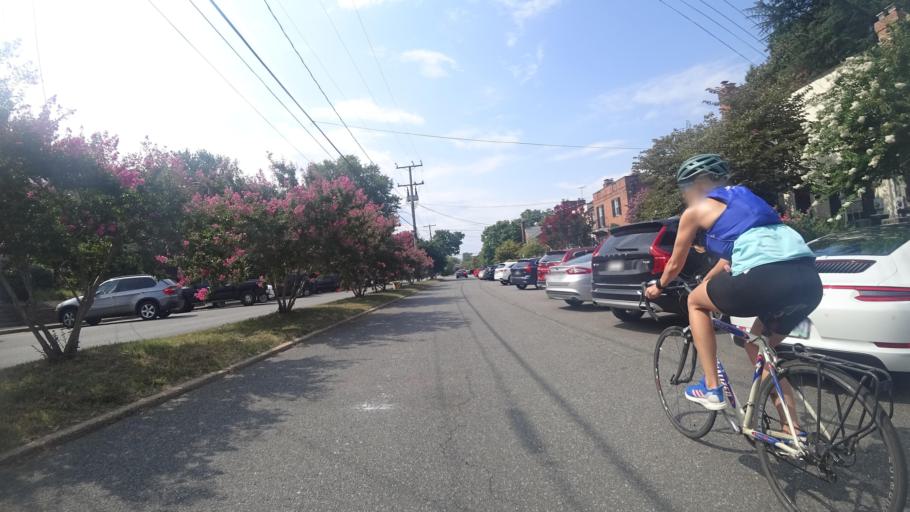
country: US
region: Virginia
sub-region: City of Alexandria
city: Alexandria
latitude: 38.7974
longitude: -77.0452
